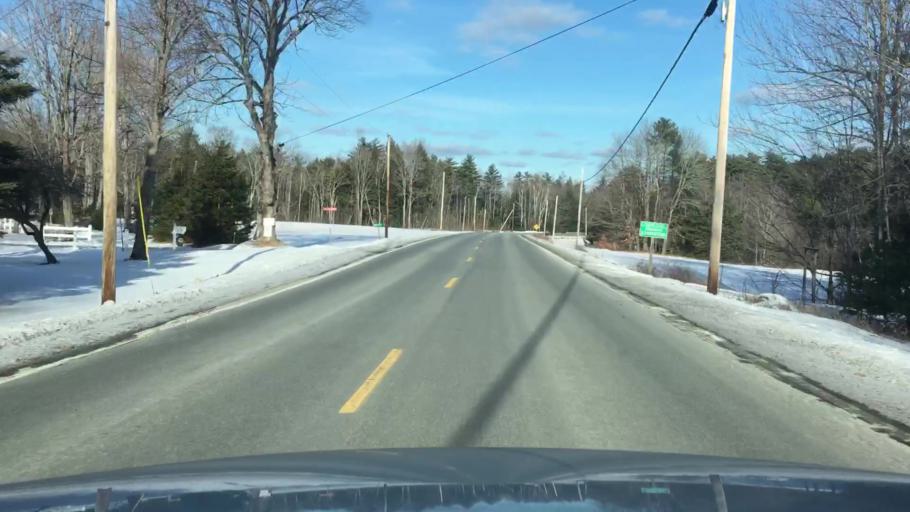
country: US
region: Maine
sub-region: Penobscot County
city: Holden
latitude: 44.7492
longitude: -68.6124
